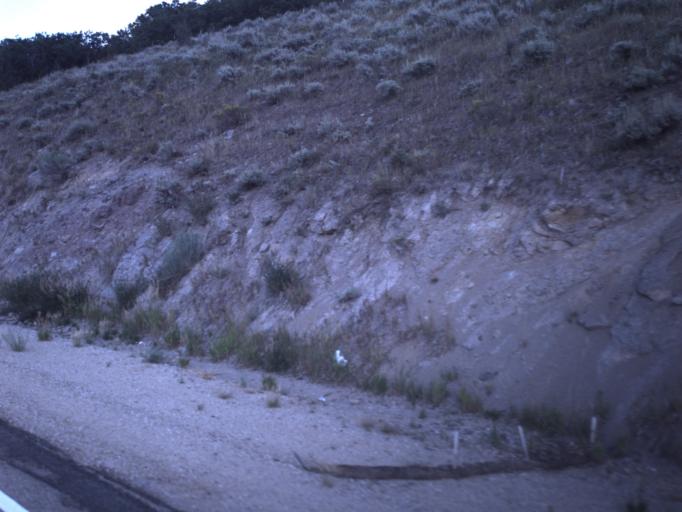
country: US
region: Utah
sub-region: Wasatch County
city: Heber
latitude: 40.5925
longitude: -111.4194
